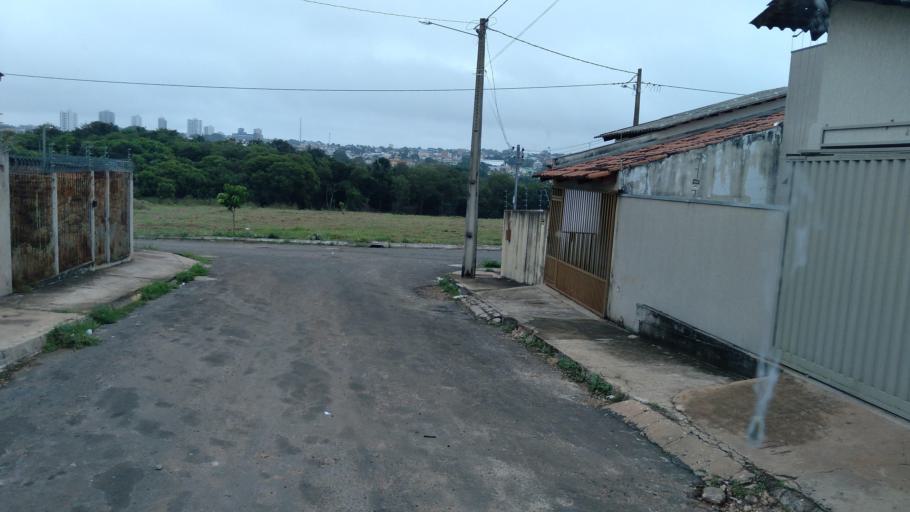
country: BR
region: Goias
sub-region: Mineiros
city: Mineiros
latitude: -17.5725
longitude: -52.5449
